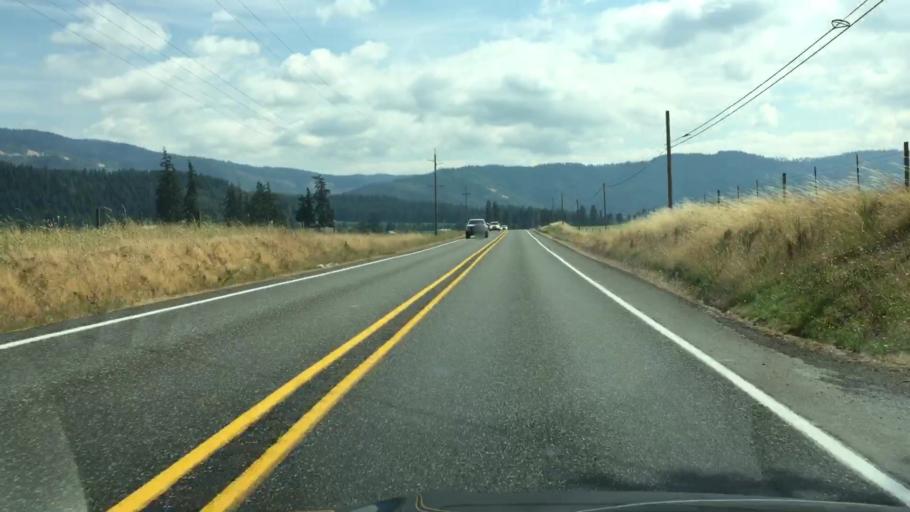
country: US
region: Washington
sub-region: Klickitat County
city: White Salmon
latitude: 45.8262
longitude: -121.4907
